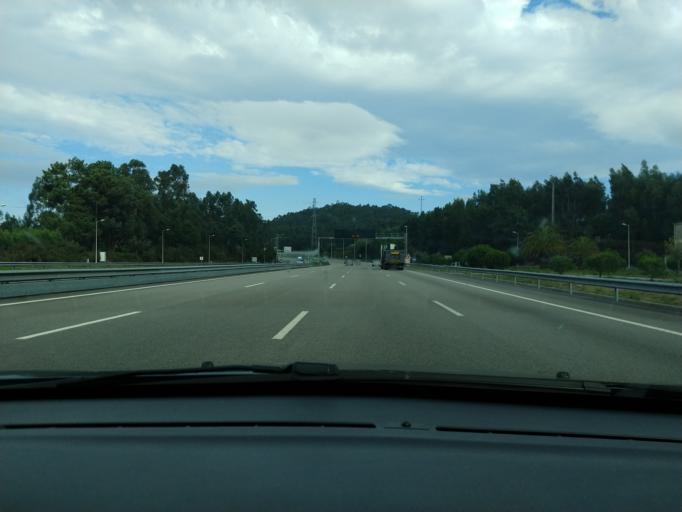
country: PT
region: Porto
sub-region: Vila Nova de Gaia
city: Grijo
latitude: 41.0465
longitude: -8.5710
